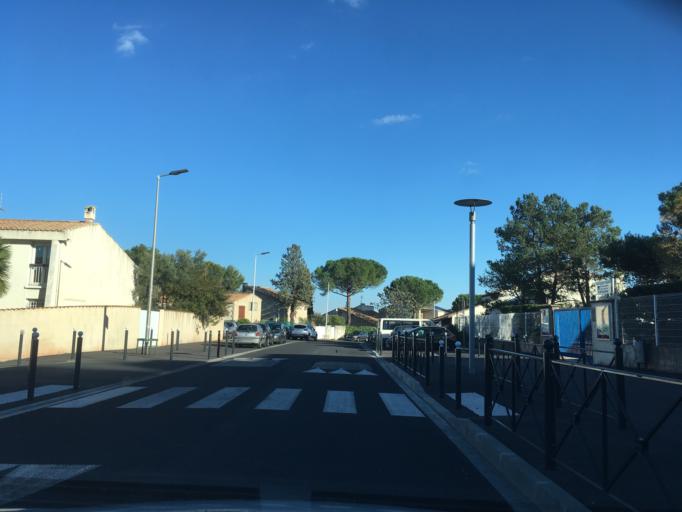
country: FR
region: Languedoc-Roussillon
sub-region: Departement de l'Herault
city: Grabels
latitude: 43.6409
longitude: 3.8195
